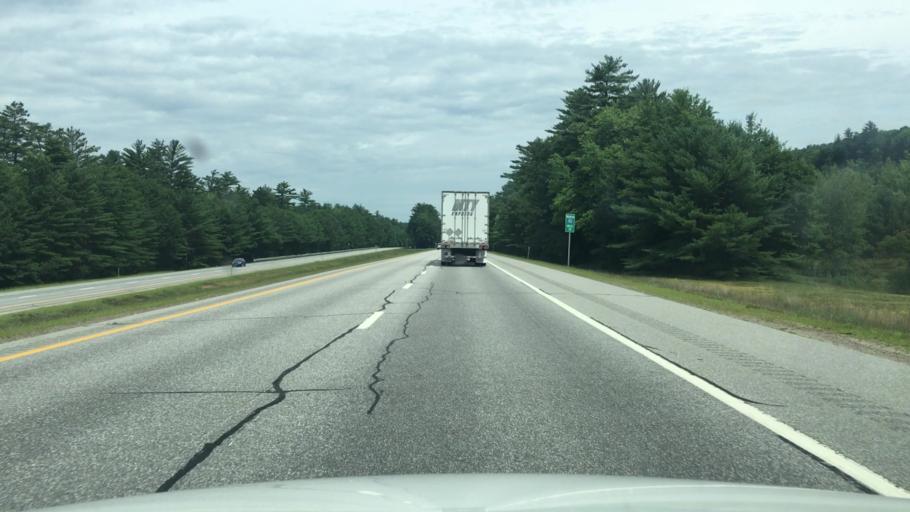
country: US
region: New Hampshire
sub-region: Grafton County
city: Ashland
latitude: 43.6511
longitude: -71.6477
